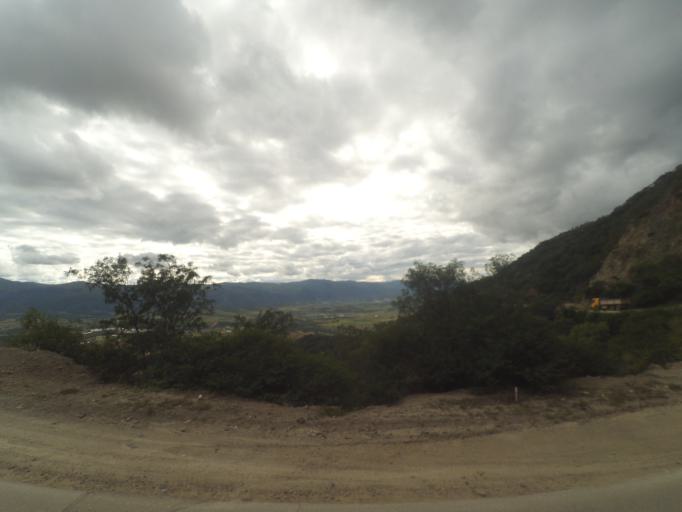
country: BO
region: Santa Cruz
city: Samaipata
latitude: -18.1712
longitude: -63.8834
